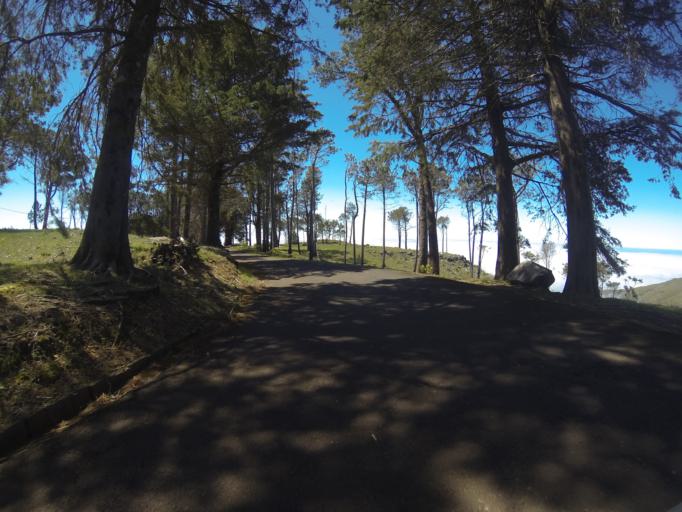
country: PT
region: Madeira
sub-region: Funchal
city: Nossa Senhora do Monte
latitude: 32.7106
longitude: -16.9120
